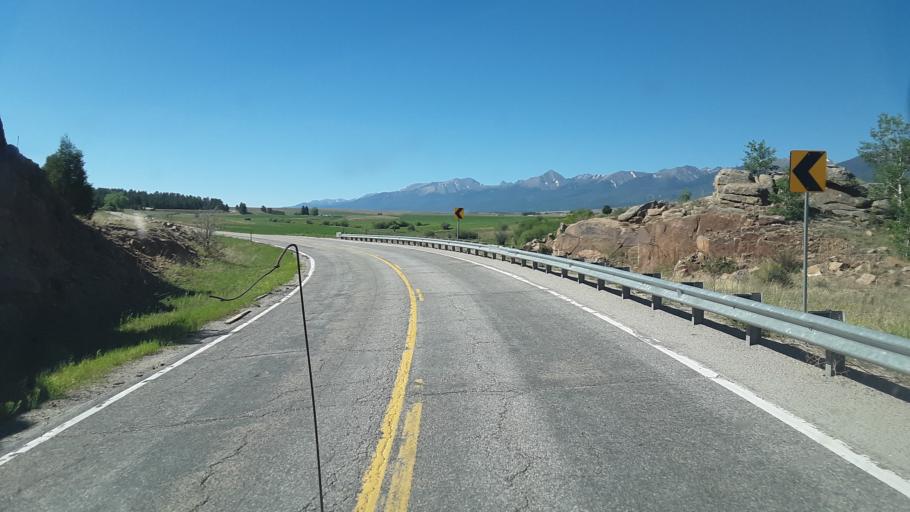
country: US
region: Colorado
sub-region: Custer County
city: Westcliffe
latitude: 38.2284
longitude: -105.5550
